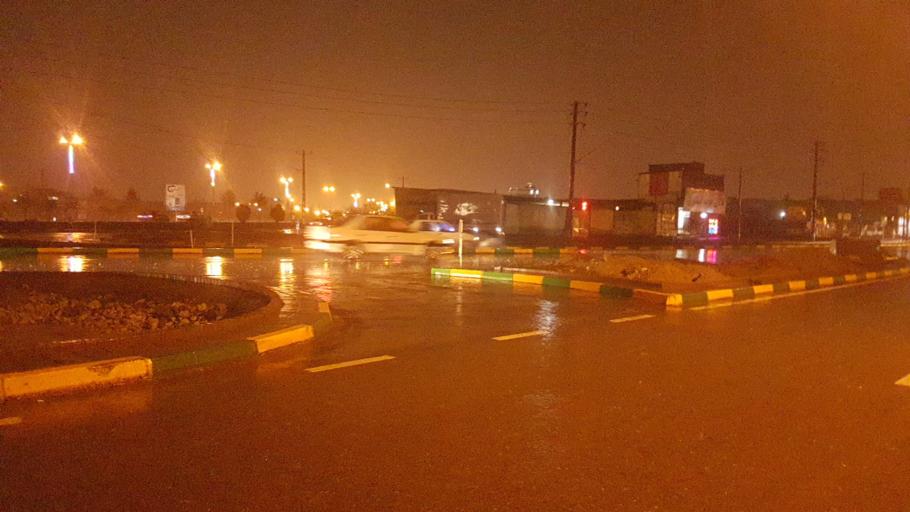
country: IR
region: Razavi Khorasan
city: Mashhad
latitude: 36.3506
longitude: 59.5758
